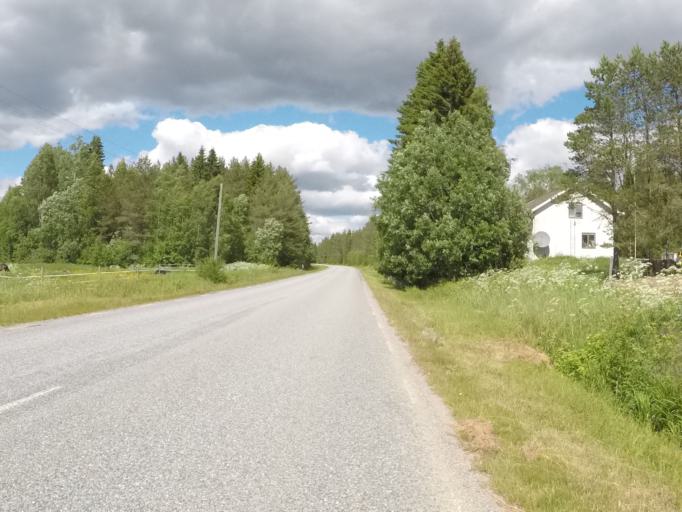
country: SE
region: Vaesterbotten
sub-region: Robertsfors Kommun
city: Robertsfors
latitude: 63.9695
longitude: 20.8122
